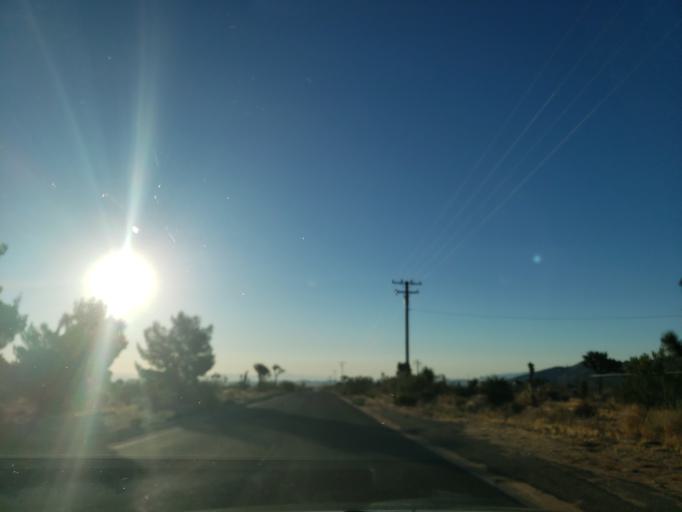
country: US
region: California
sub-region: San Bernardino County
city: Joshua Tree
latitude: 34.1930
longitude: -116.3759
